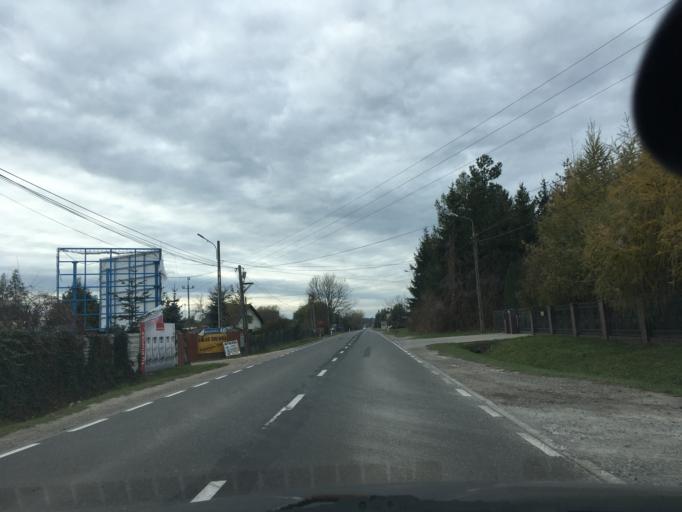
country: PL
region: Masovian Voivodeship
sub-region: Powiat piaseczynski
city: Tarczyn
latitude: 51.9789
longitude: 20.8508
